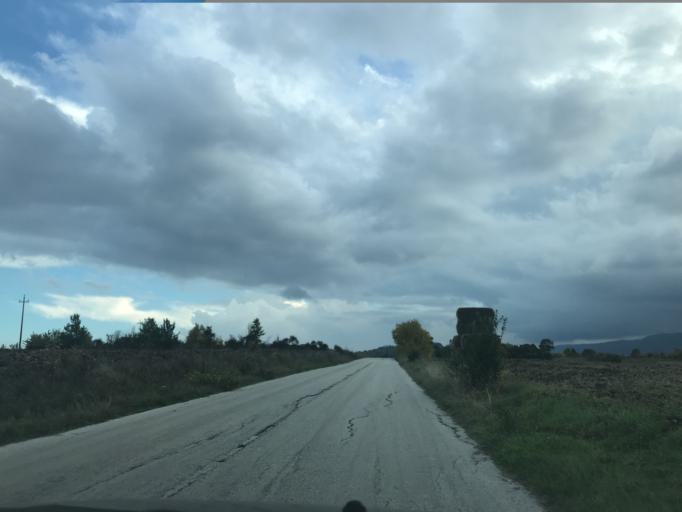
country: IT
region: Molise
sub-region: Provincia di Isernia
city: Bagnoli del Trigno
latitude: 41.6903
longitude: 14.4620
